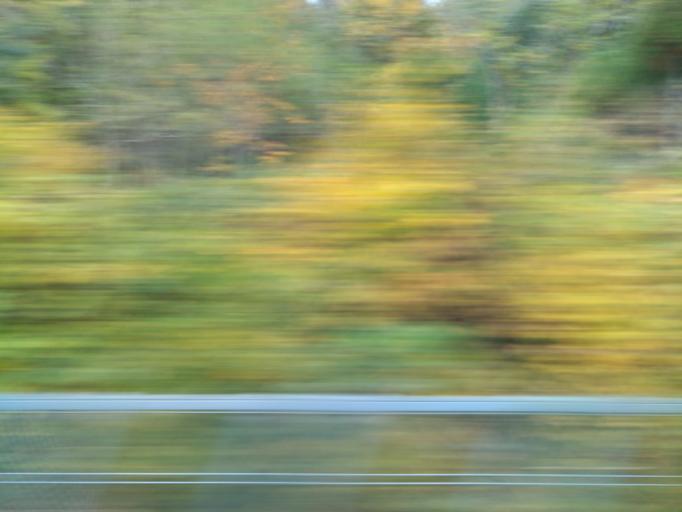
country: JP
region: Aomori
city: Goshogawara
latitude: 41.1543
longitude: 140.5070
